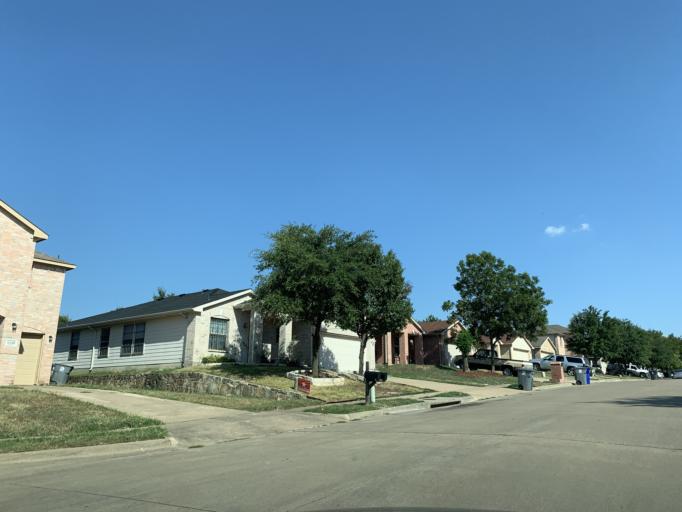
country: US
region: Texas
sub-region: Dallas County
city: Hutchins
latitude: 32.6679
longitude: -96.7688
